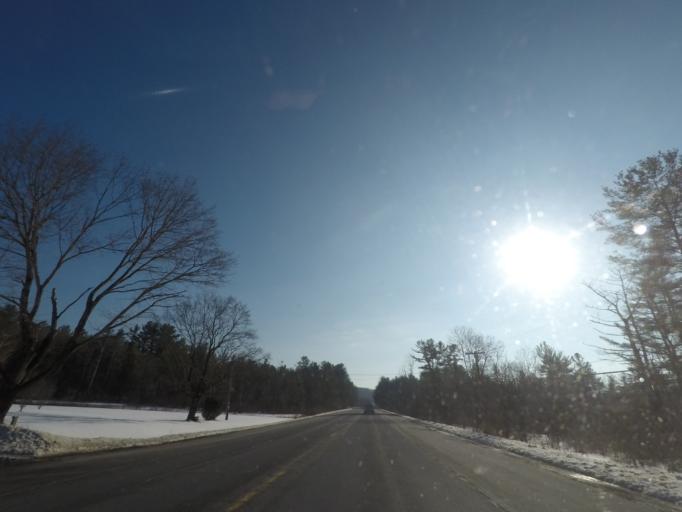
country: US
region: Massachusetts
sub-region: Berkshire County
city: Lanesborough
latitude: 42.5238
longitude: -73.3575
